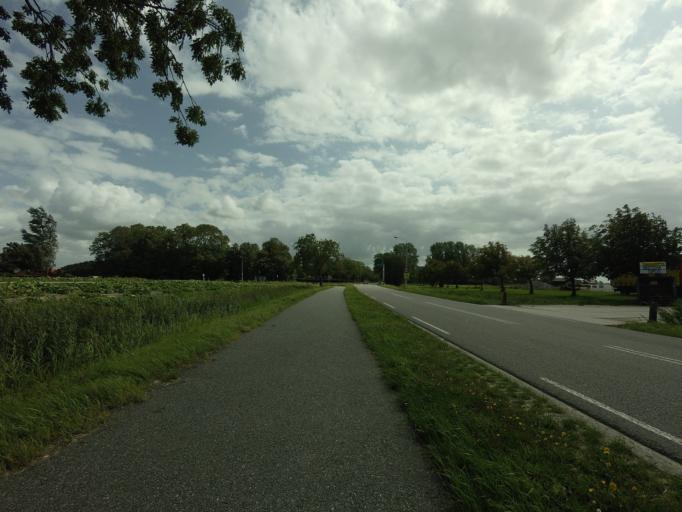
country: NL
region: Friesland
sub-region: Gemeente Harlingen
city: Harlingen
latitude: 53.1340
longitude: 5.4692
